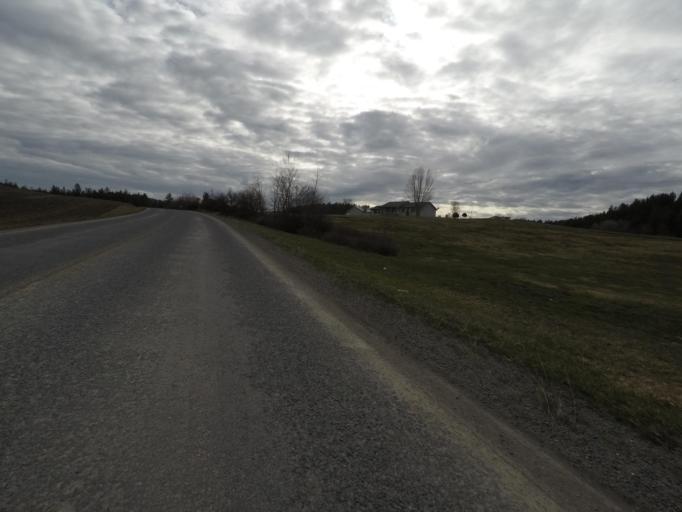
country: US
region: Washington
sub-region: Stevens County
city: Colville
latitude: 48.5182
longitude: -117.8739
